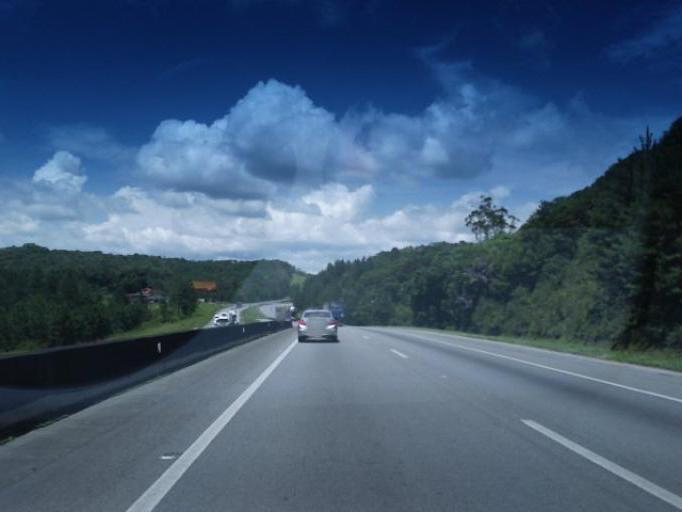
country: BR
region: Sao Paulo
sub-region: Juquitiba
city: Juquitiba
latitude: -23.9520
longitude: -47.1037
